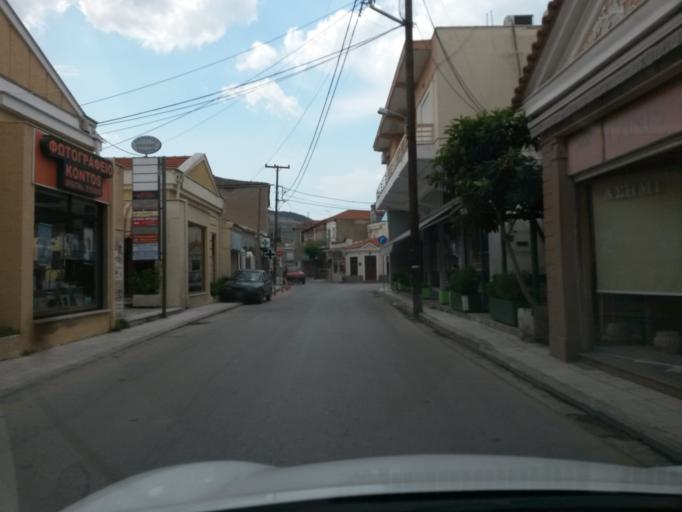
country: GR
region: North Aegean
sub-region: Nomos Lesvou
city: Kalloni
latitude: 39.2329
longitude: 26.2090
